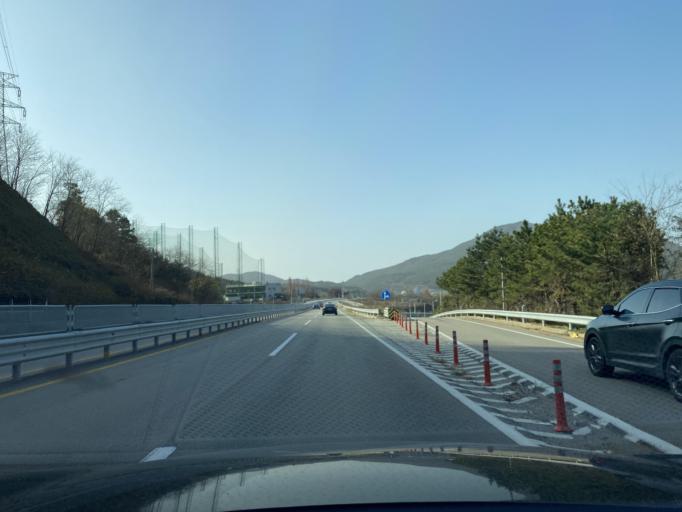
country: KR
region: Chungcheongnam-do
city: Hongsung
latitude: 36.6848
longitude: 126.6603
